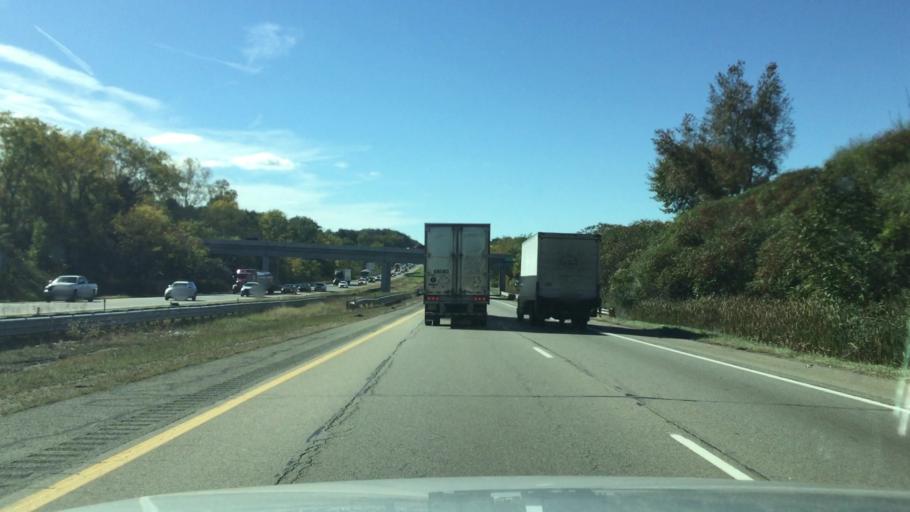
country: US
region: Michigan
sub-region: Washtenaw County
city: Dexter
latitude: 42.2978
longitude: -83.8964
